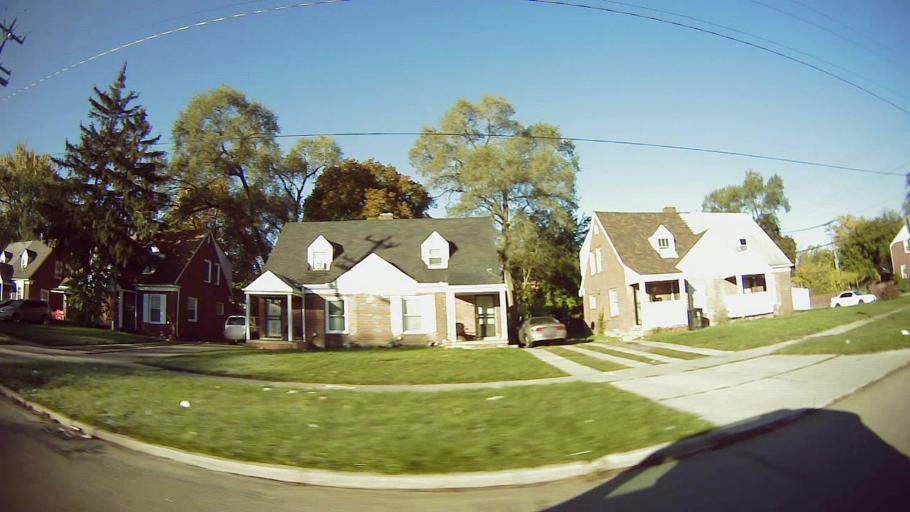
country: US
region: Michigan
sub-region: Oakland County
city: Oak Park
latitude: 42.4404
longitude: -83.1709
